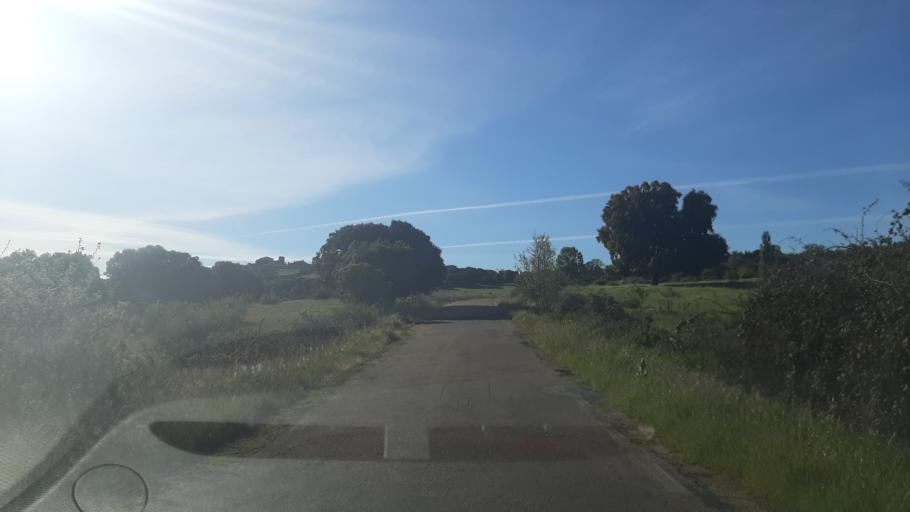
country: ES
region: Castille and Leon
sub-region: Provincia de Salamanca
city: Guijo de Avila
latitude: 40.5345
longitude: -5.6492
